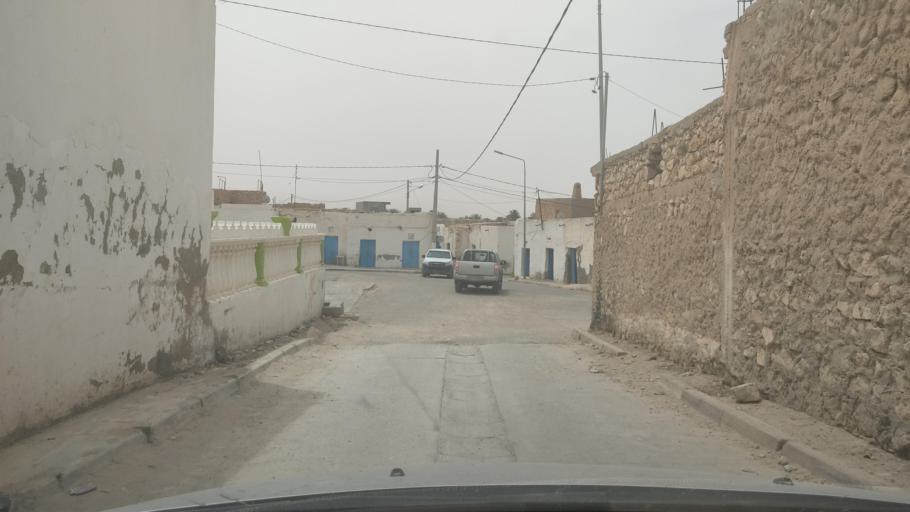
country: TN
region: Gafsa
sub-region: Gafsa Municipality
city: Gafsa
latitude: 34.3347
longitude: 8.9521
